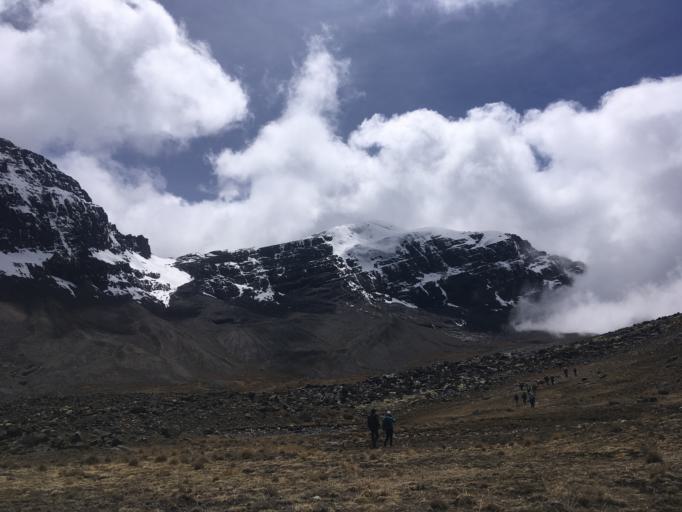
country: BO
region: La Paz
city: La Paz
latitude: -16.3965
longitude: -67.9596
